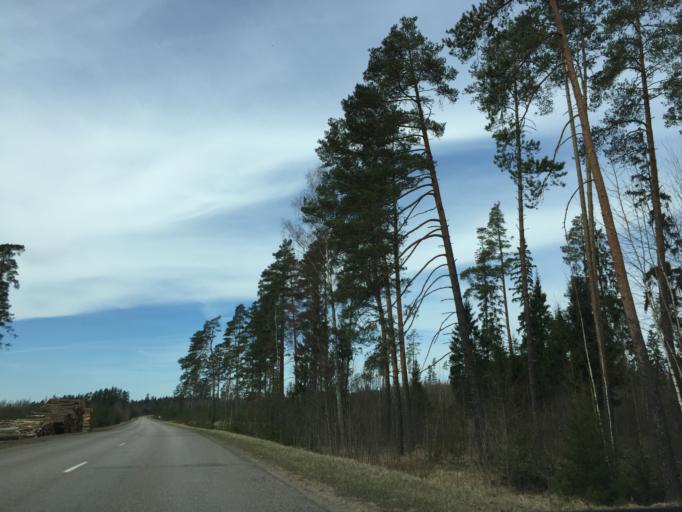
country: LV
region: Valkas Rajons
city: Valka
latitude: 57.8011
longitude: 25.8524
